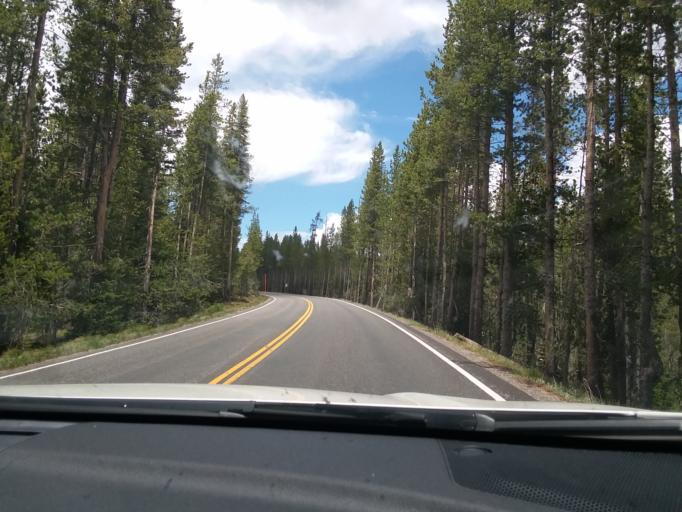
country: US
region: Idaho
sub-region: Teton County
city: Driggs
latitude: 44.1491
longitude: -110.6702
